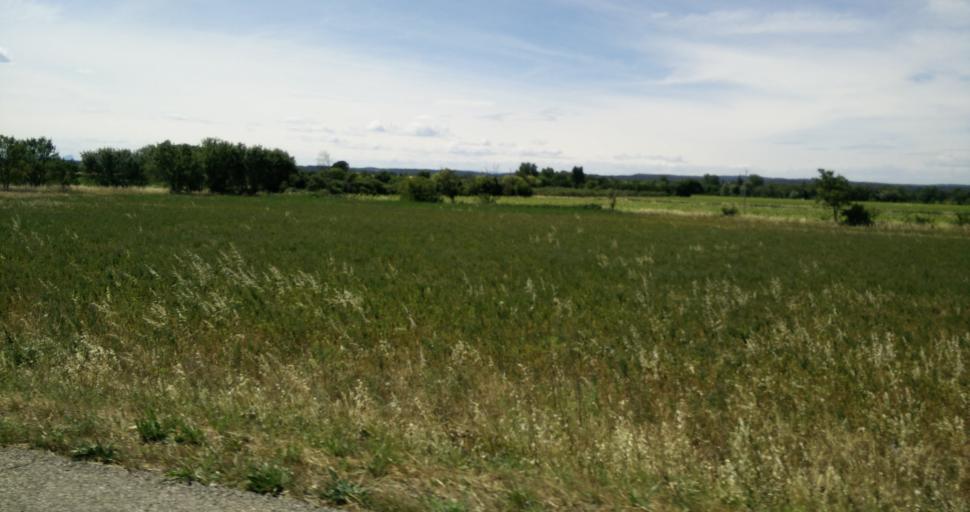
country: FR
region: Languedoc-Roussillon
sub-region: Departement du Gard
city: Aubord
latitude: 43.7434
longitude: 4.2967
